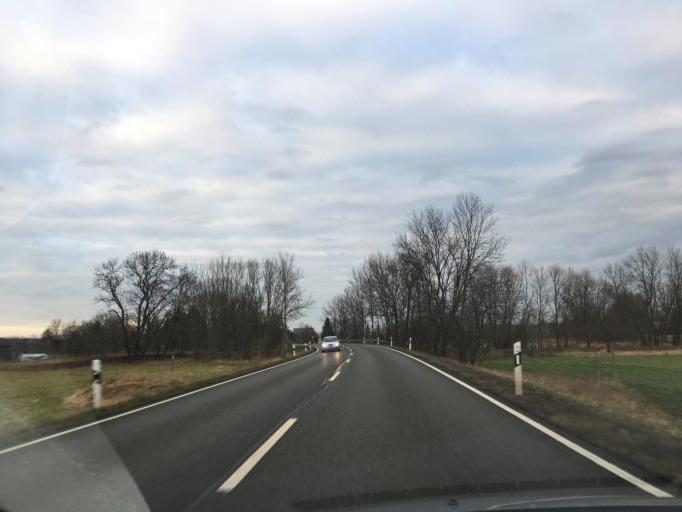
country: DE
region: Thuringia
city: Fockendorf
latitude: 51.0457
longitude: 12.4554
